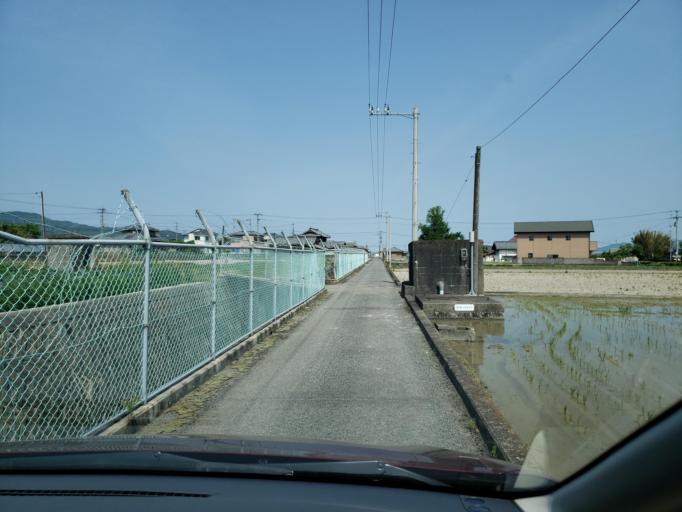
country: JP
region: Tokushima
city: Wakimachi
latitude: 34.0910
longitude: 134.2408
